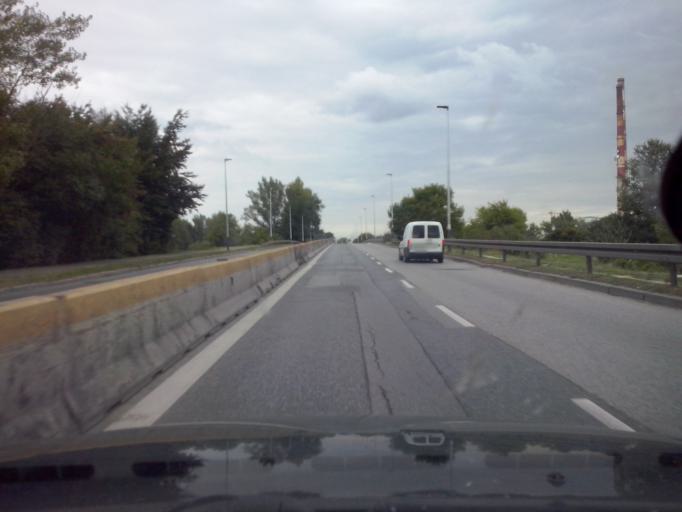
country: PL
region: Lesser Poland Voivodeship
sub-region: Krakow
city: Krakow
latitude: 50.0532
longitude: 19.9916
